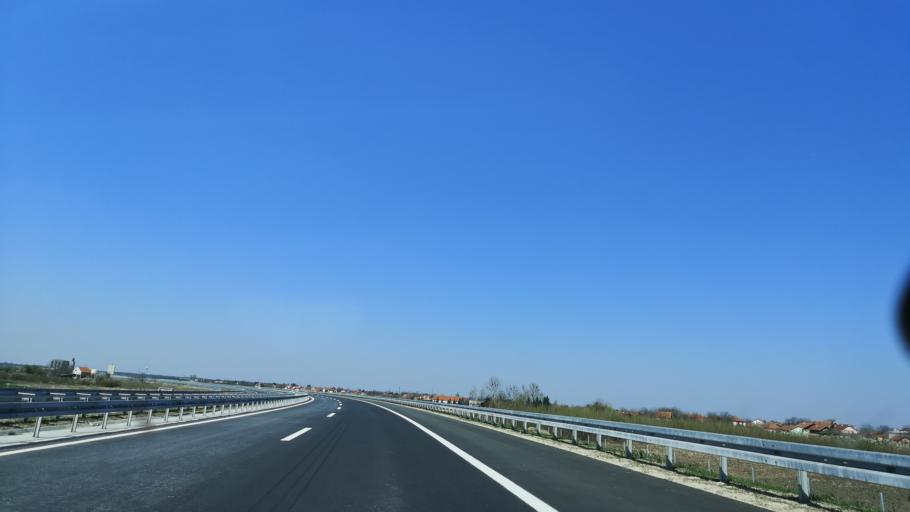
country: RS
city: Boljevci
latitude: 44.7480
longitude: 20.2502
